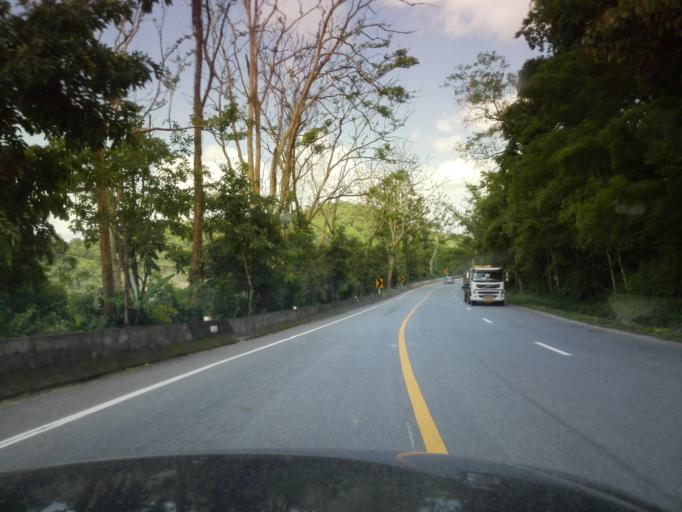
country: TH
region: Tak
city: Mae Sot
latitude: 16.7690
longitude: 98.7114
